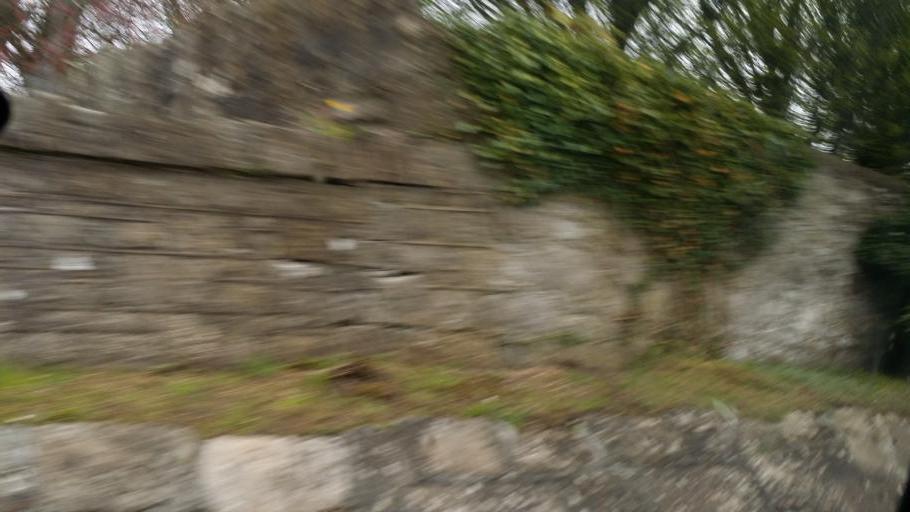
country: IE
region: Ulster
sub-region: An Cabhan
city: Ballyconnell
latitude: 54.1174
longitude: -7.5869
